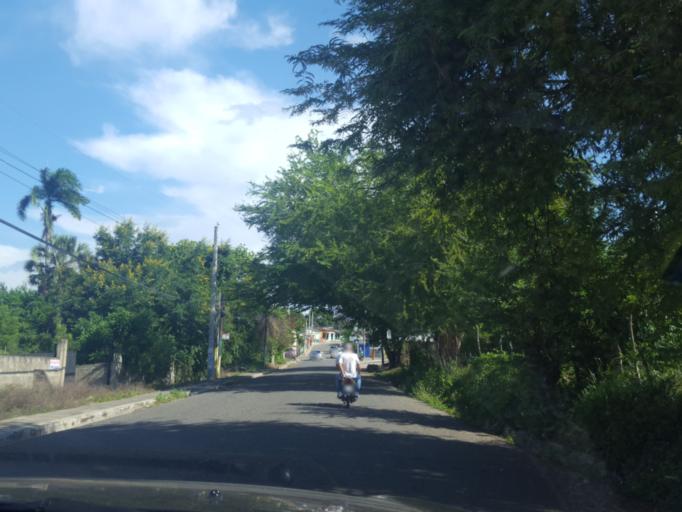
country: DO
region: La Vega
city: Rio Verde Arriba
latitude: 19.3640
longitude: -70.6051
